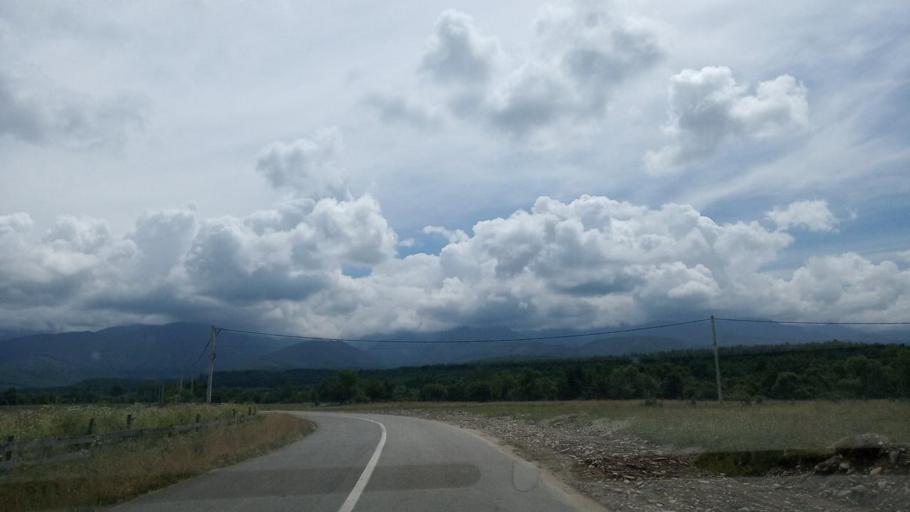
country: RO
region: Sibiu
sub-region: Comuna Porumbacu de Jos
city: Porumbacu de Jos
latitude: 45.7071
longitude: 24.4808
